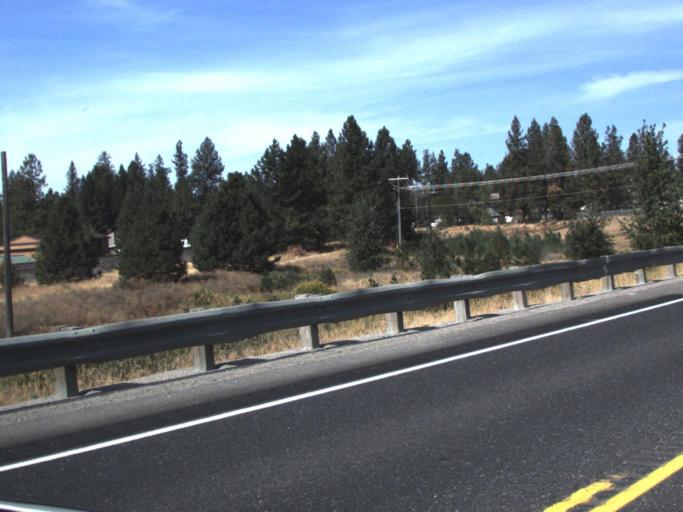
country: US
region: Washington
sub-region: Spokane County
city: Deer Park
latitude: 48.0573
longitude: -117.6187
